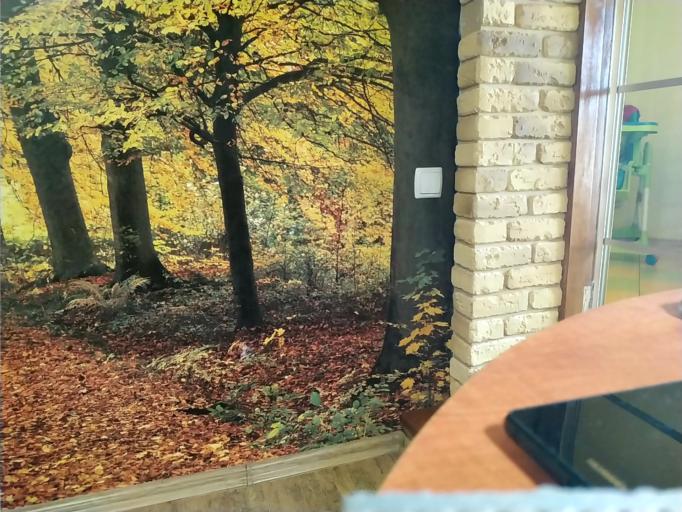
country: RU
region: Kaluga
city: Kondrovo
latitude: 54.8143
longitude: 35.9497
